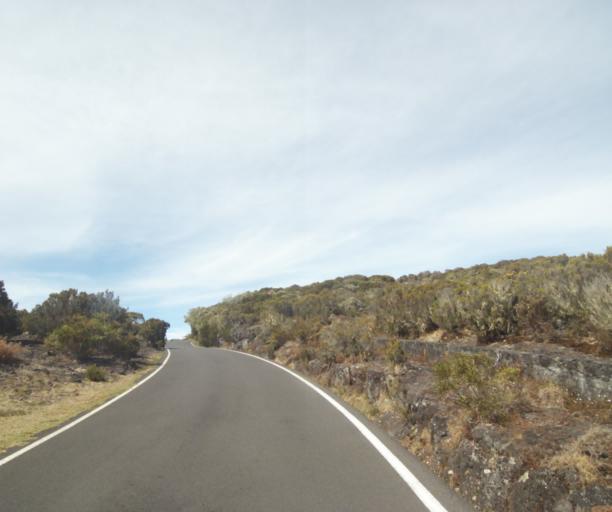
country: RE
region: Reunion
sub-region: Reunion
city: Trois-Bassins
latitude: -21.0728
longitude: 55.3817
